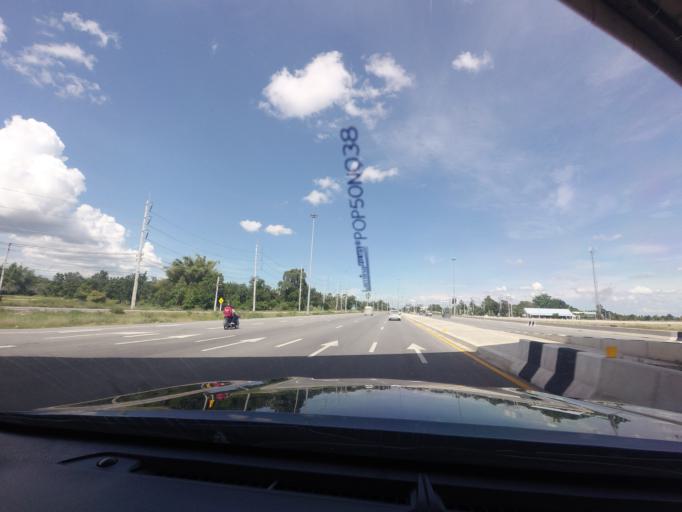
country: TH
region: Kanchanaburi
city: Kanchanaburi
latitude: 14.0436
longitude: 99.6042
